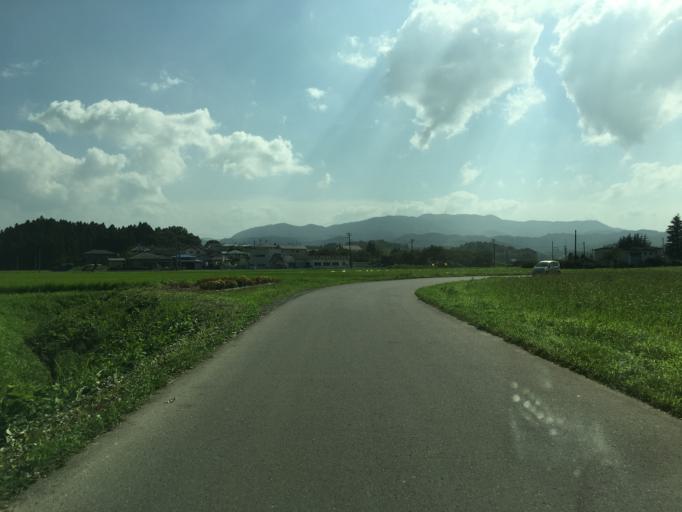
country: JP
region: Miyagi
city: Kakuda
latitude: 37.9460
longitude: 140.7751
